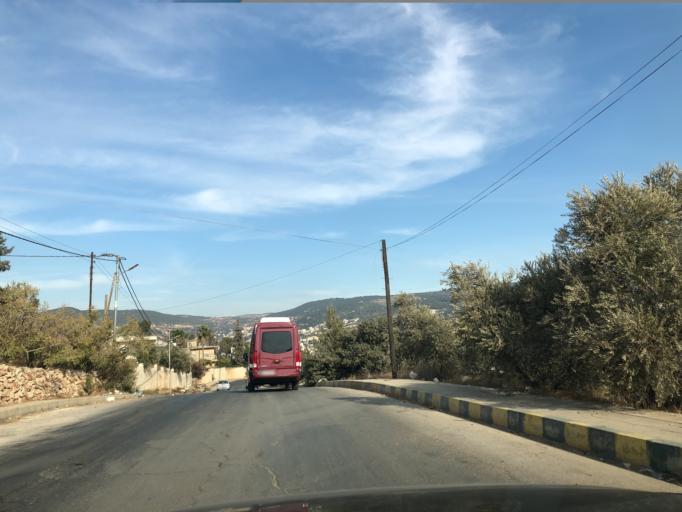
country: JO
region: Ajlun
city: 'Ajlun
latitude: 32.3295
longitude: 35.7357
